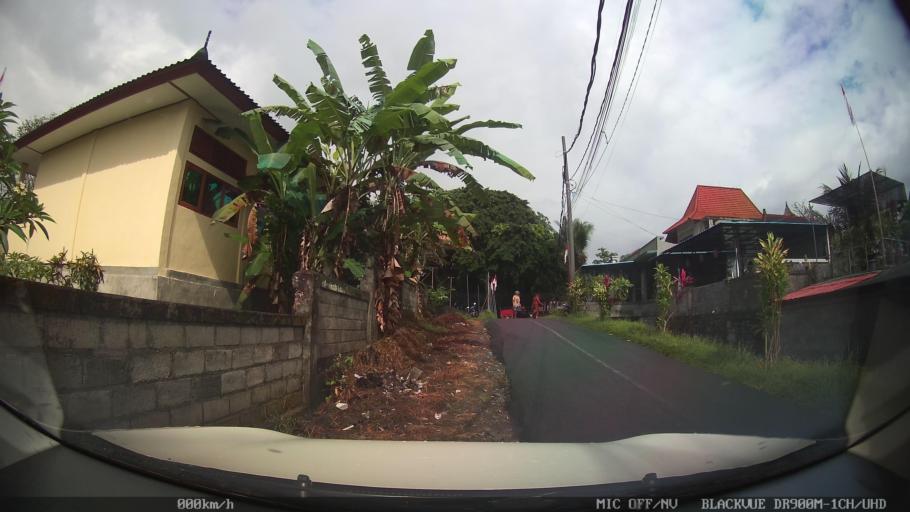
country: ID
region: Bali
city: Banjar Tebongkang
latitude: -8.5441
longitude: 115.2504
